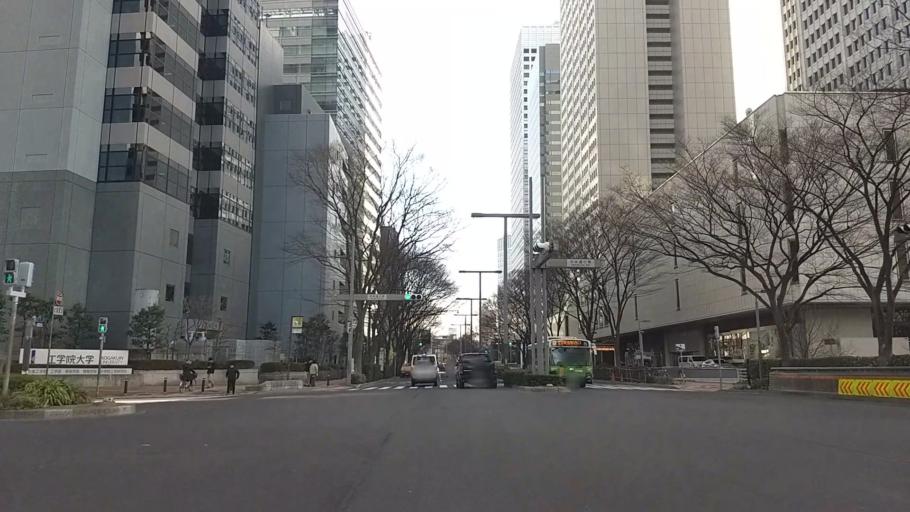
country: JP
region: Tokyo
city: Tokyo
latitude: 35.6912
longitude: 139.6948
